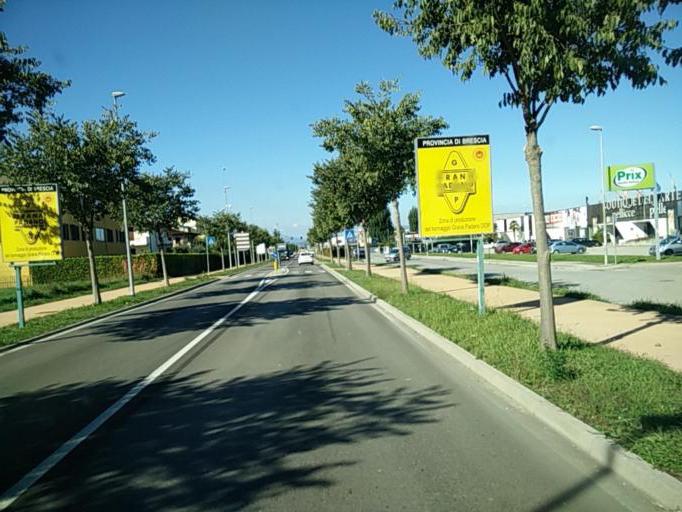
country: IT
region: Lombardy
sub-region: Provincia di Brescia
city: San Martino della Battaglia
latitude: 45.4398
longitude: 10.6022
